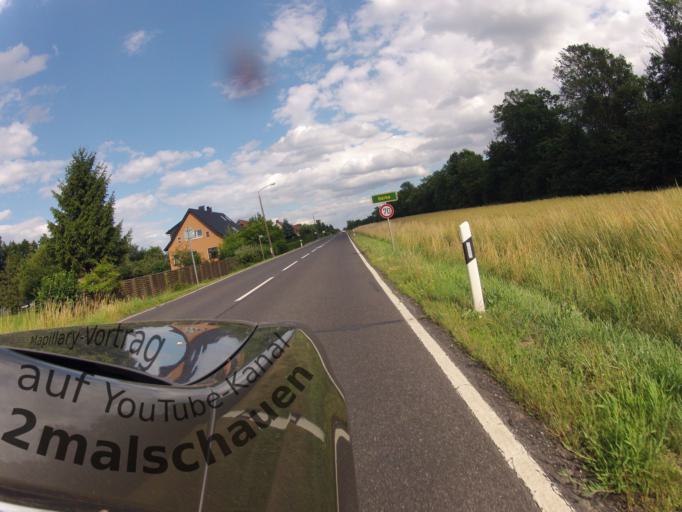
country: DE
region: Mecklenburg-Vorpommern
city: Seebad Bansin
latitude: 53.8873
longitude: 14.0878
